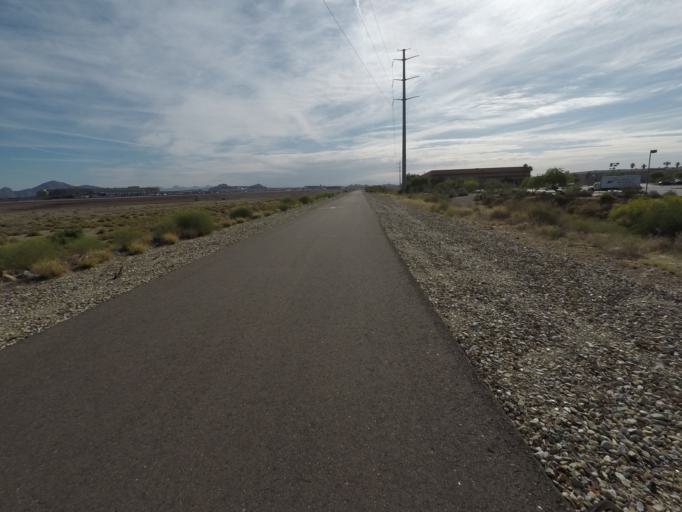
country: US
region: Arizona
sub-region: Maricopa County
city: Tempe Junction
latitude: 33.4239
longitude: -112.0052
